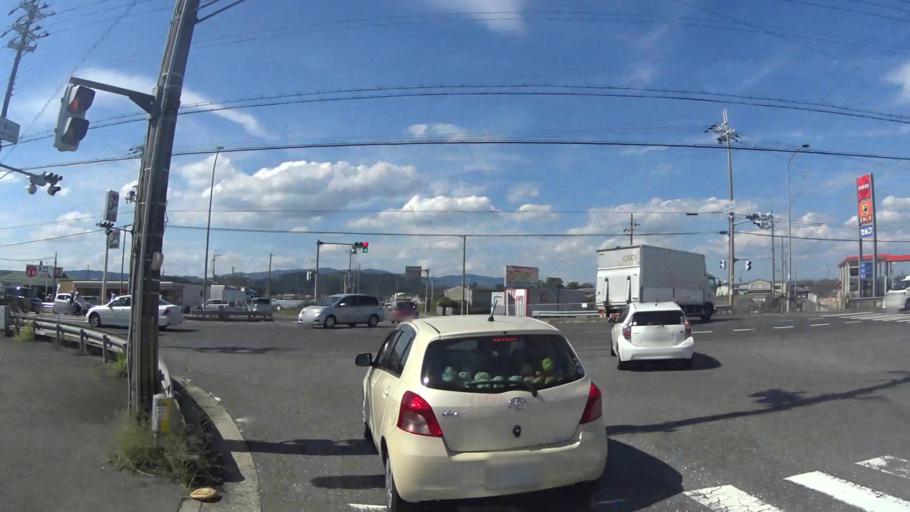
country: JP
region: Kyoto
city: Yawata
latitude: 34.8627
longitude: 135.7203
